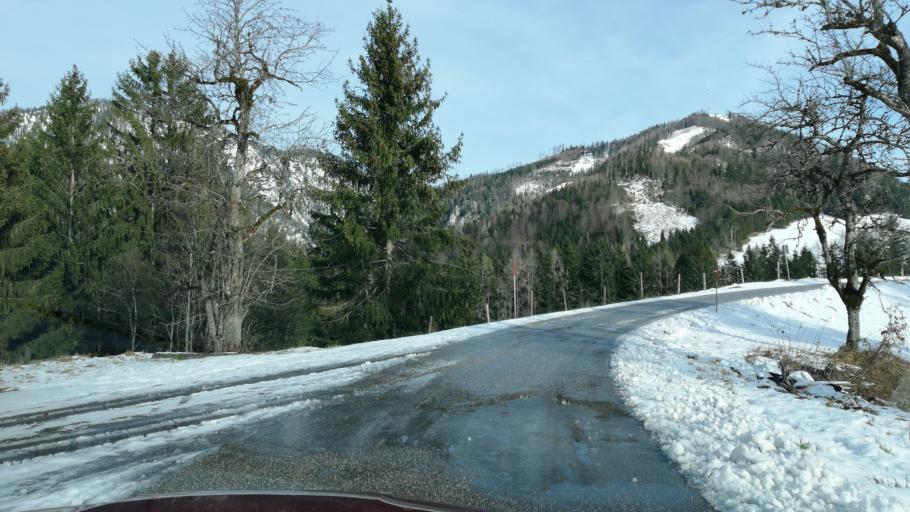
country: AT
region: Upper Austria
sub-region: Politischer Bezirk Kirchdorf an der Krems
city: Rossleithen
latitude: 47.7271
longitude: 14.3442
